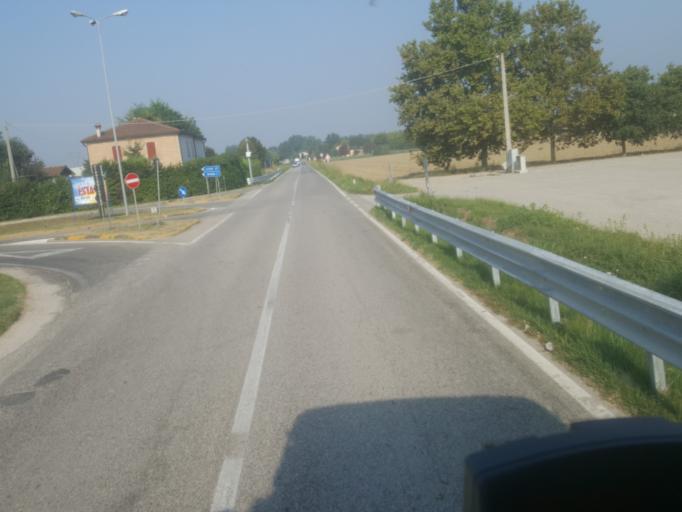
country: IT
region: Emilia-Romagna
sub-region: Provincia di Ravenna
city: Voltana
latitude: 44.5526
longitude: 11.9445
